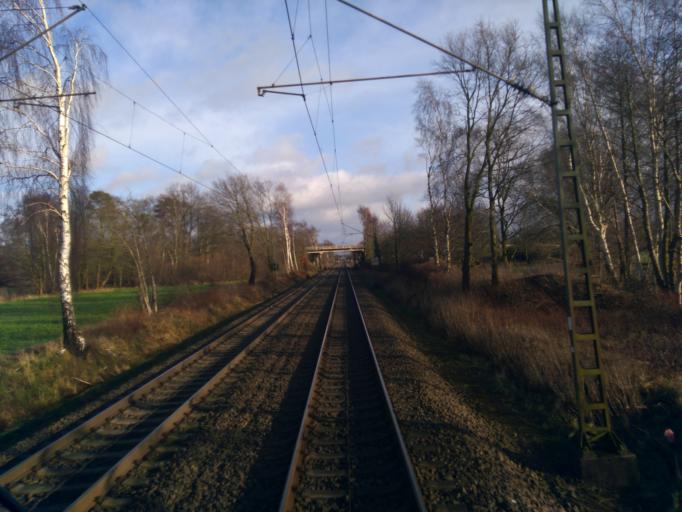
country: DE
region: Lower Saxony
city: Botersen
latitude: 53.1053
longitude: 9.3334
